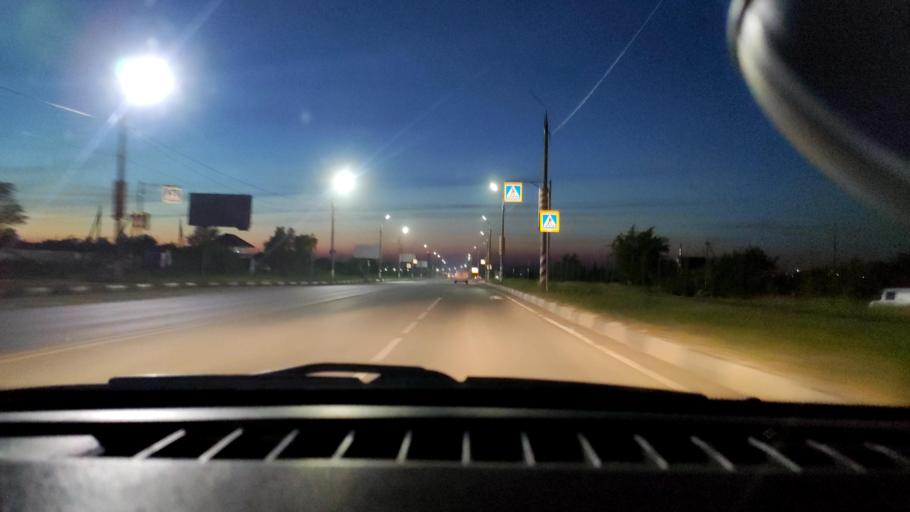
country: RU
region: Samara
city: Novokuybyshevsk
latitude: 53.0770
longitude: 49.9977
